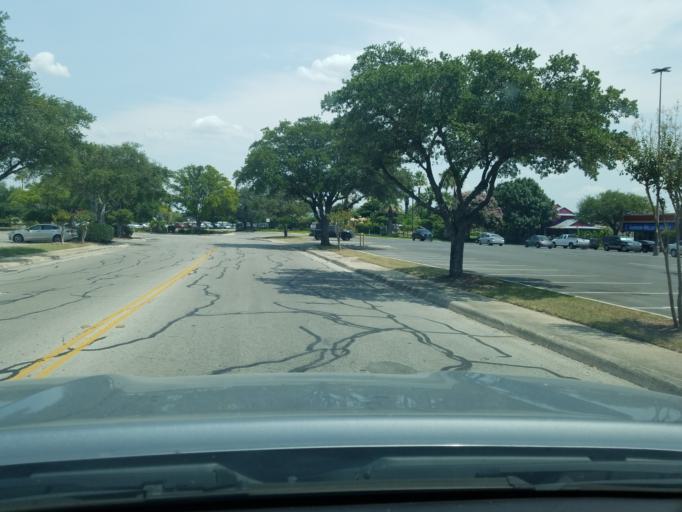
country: US
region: Texas
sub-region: Bexar County
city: Hollywood Park
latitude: 29.5640
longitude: -98.4872
